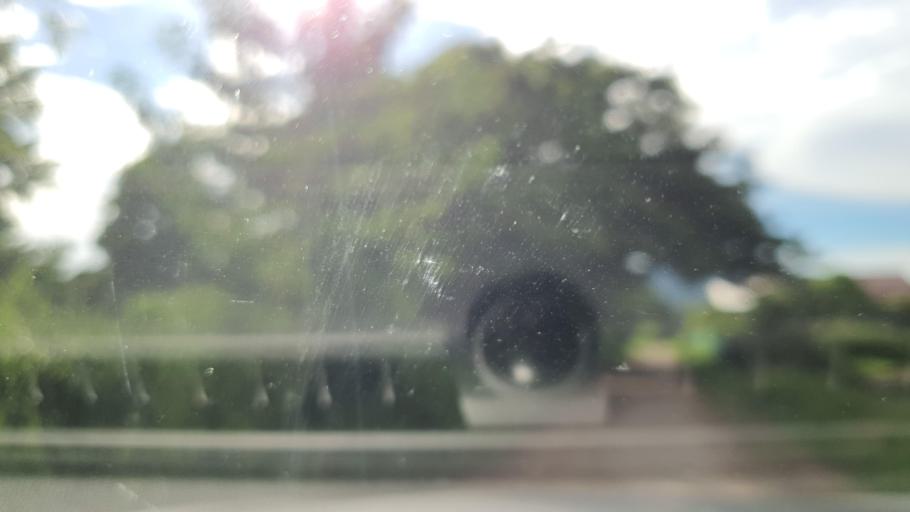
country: TH
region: Chiang Mai
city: Mae On
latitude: 18.7595
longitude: 99.2623
